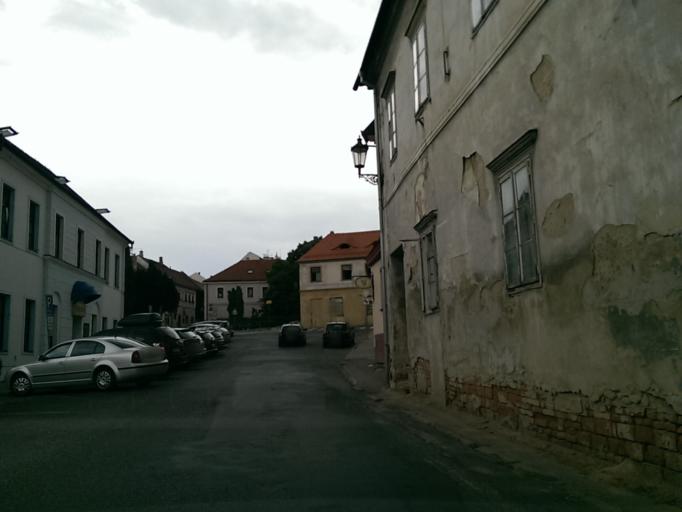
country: CZ
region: South Moravian
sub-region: Okres Breclav
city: Mikulov
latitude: 48.8077
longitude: 16.6393
